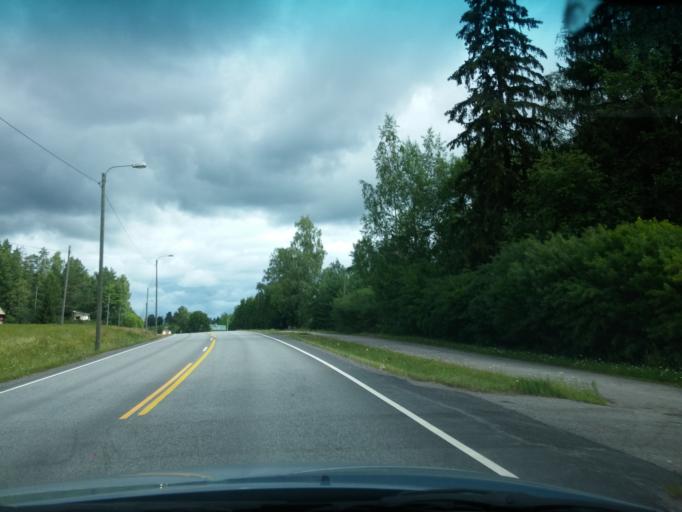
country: FI
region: Uusimaa
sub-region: Porvoo
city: Askola
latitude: 60.5128
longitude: 25.5769
